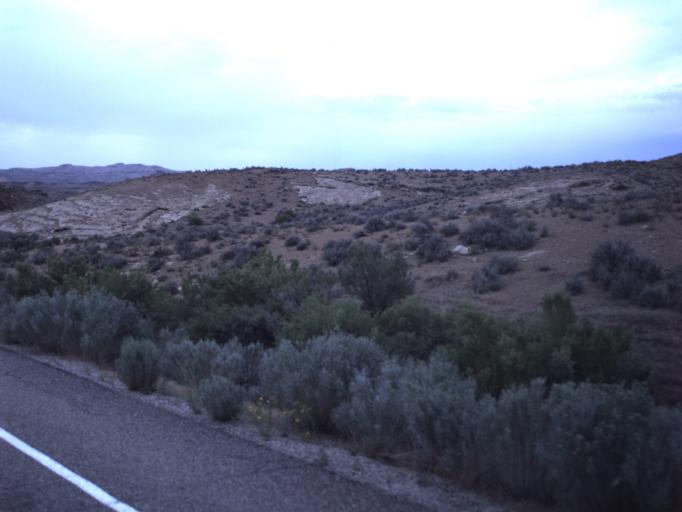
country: US
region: Colorado
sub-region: Rio Blanco County
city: Rangely
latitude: 39.9644
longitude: -109.1644
